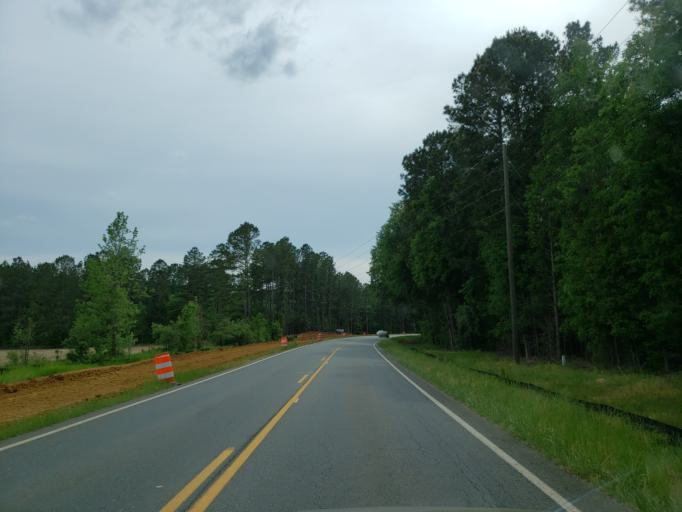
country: US
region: Georgia
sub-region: Macon County
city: Marshallville
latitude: 32.3805
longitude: -83.8812
